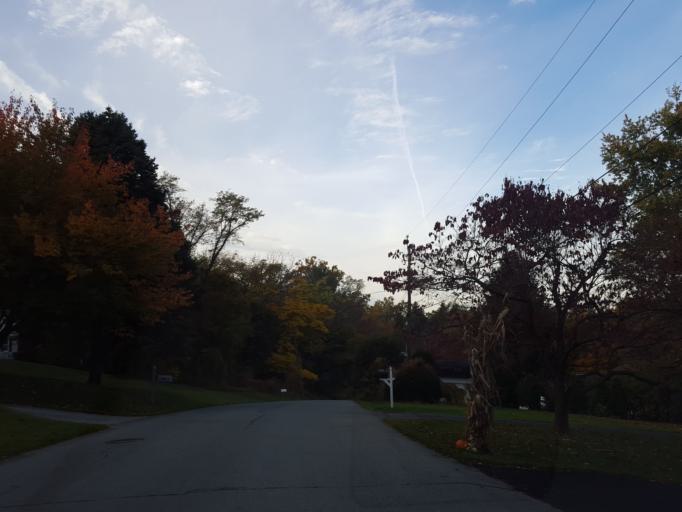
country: US
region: Pennsylvania
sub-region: York County
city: Stonybrook
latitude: 39.9739
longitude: -76.6345
